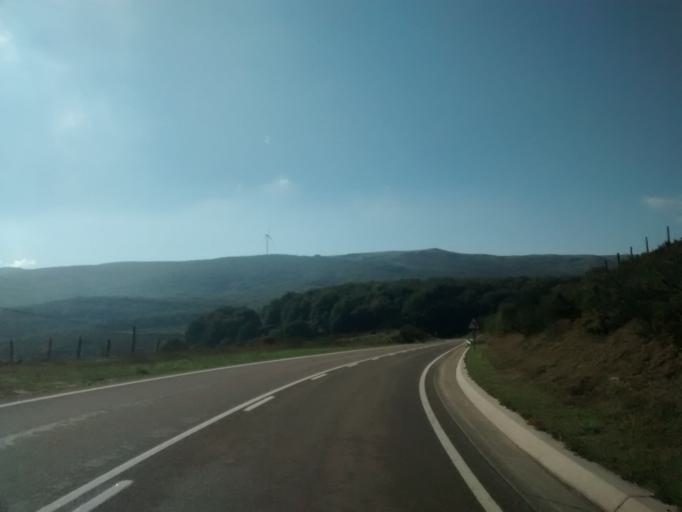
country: ES
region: Cantabria
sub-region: Provincia de Cantabria
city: Reinosa
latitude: 42.9820
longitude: -4.1041
